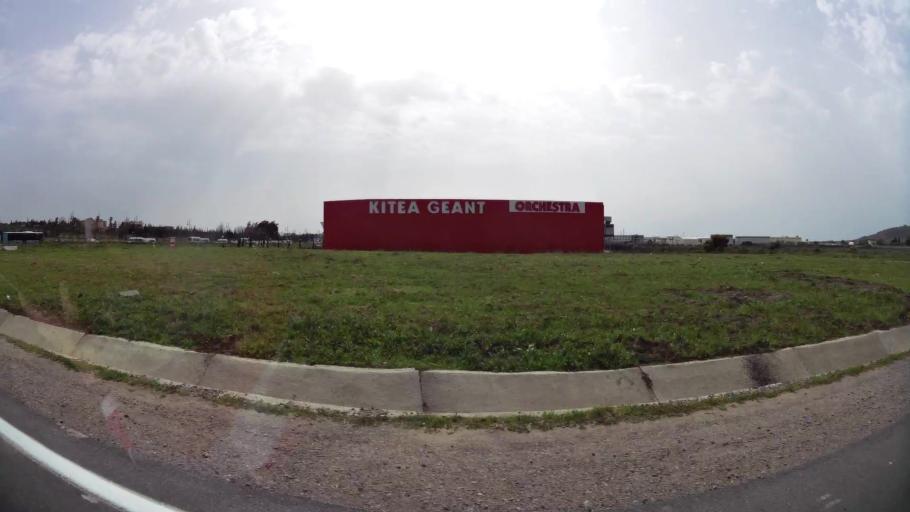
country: MA
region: Tanger-Tetouan
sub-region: Tanger-Assilah
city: Boukhalef
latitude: 35.7255
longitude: -5.8953
